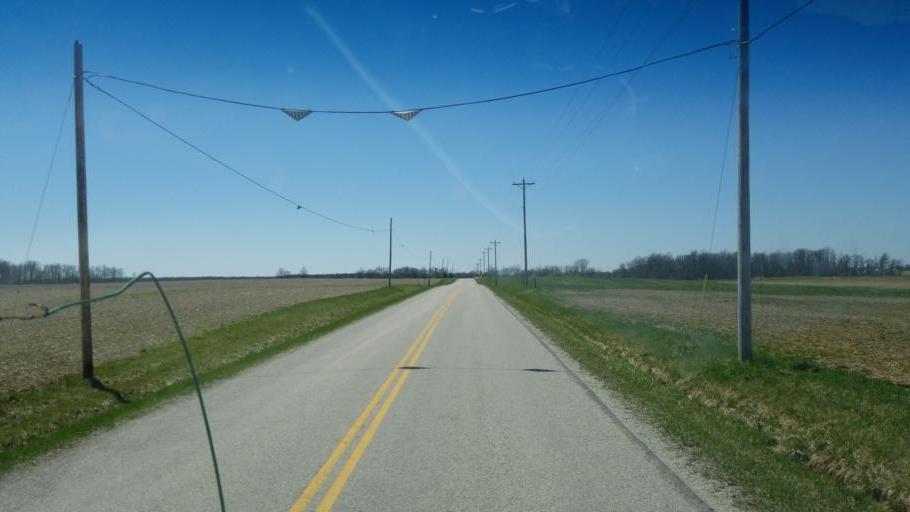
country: US
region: Ohio
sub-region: Huron County
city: Willard
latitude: 41.0530
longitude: -82.8972
